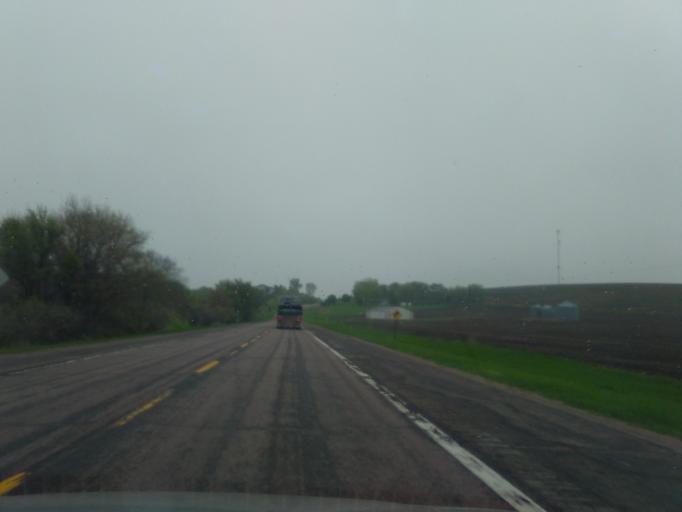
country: US
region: Nebraska
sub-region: Burt County
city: Oakland
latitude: 41.8167
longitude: -96.4724
